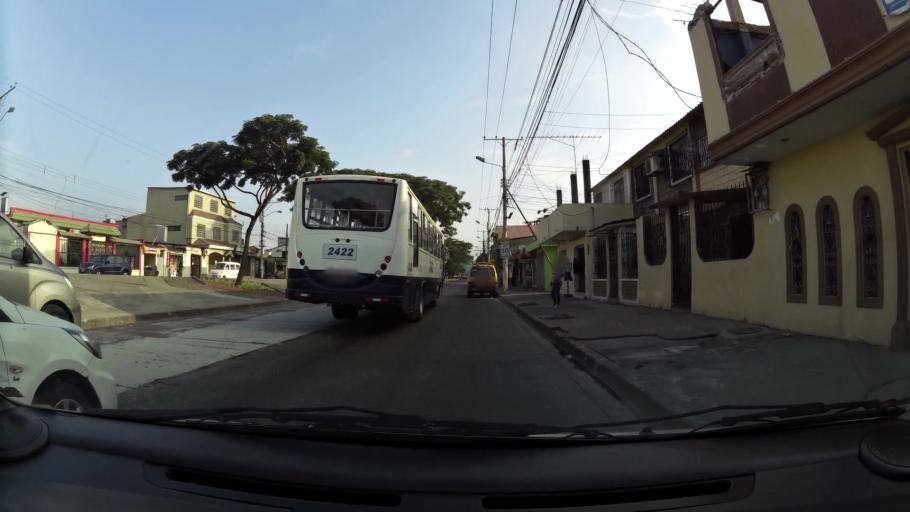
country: EC
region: Guayas
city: Eloy Alfaro
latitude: -2.1302
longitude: -79.9023
